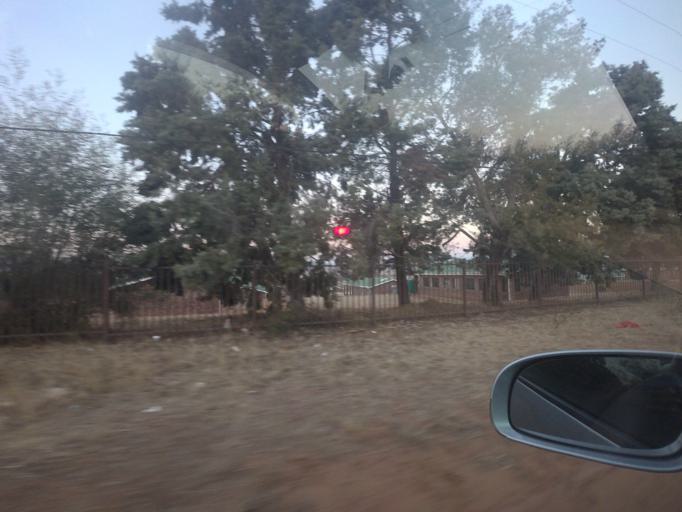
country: LS
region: Leribe
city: Leribe
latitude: -28.8779
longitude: 28.0554
